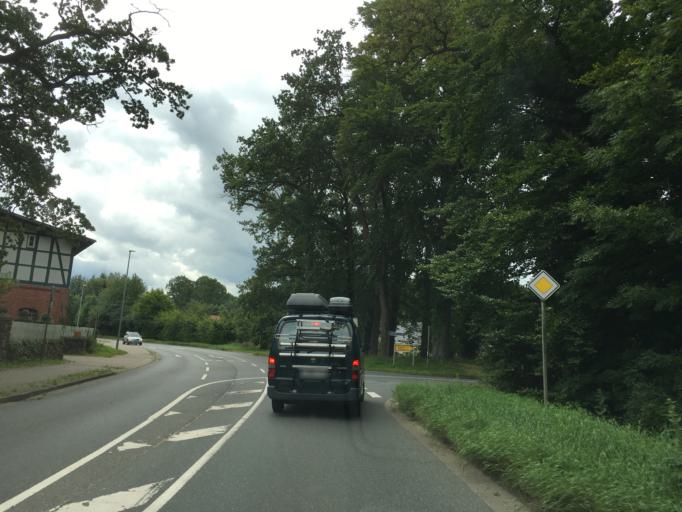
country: DE
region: Lower Saxony
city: Embsen
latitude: 53.2132
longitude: 10.3686
